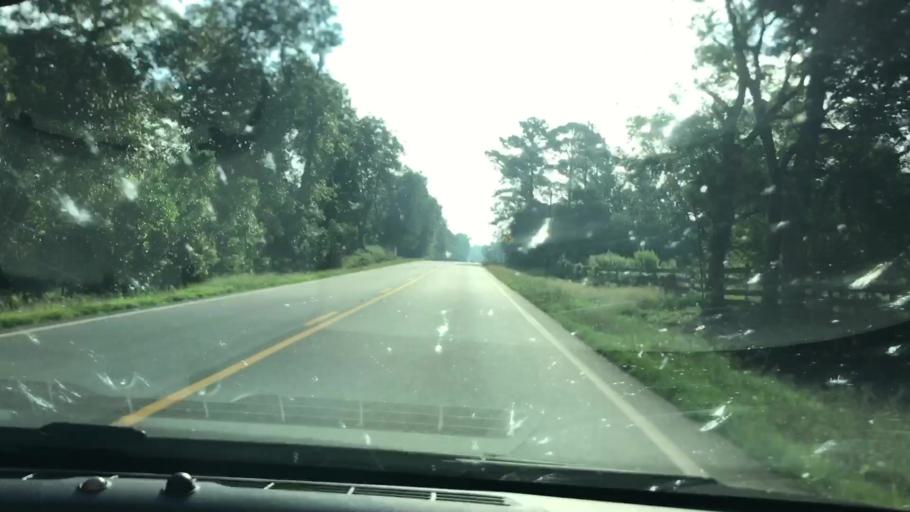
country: US
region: Georgia
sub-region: Terrell County
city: Dawson
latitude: 31.7696
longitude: -84.4733
